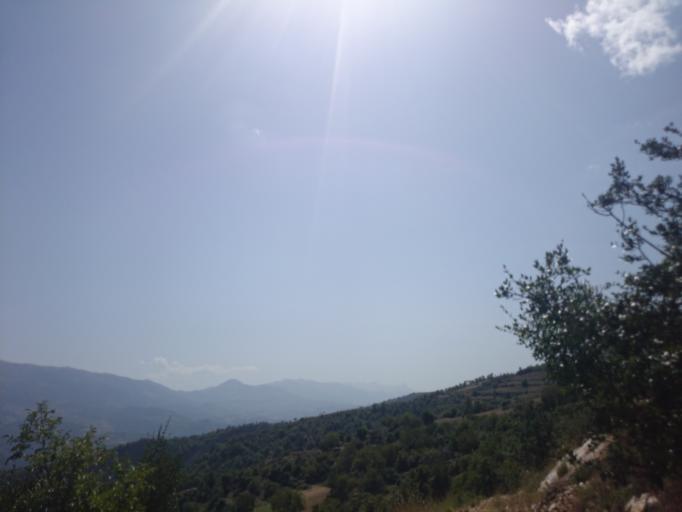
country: AL
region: Elbasan
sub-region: Rrethi i Gramshit
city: Kushove
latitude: 40.7512
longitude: 20.1648
